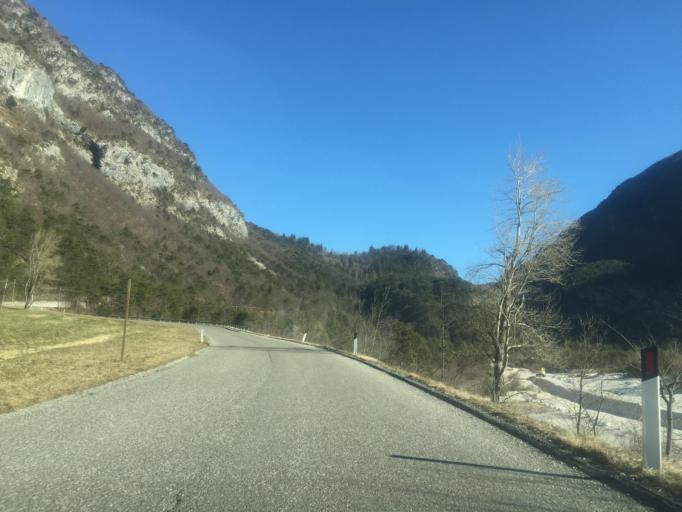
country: IT
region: Friuli Venezia Giulia
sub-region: Provincia di Udine
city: Tolmezzo
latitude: 46.4070
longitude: 13.0421
